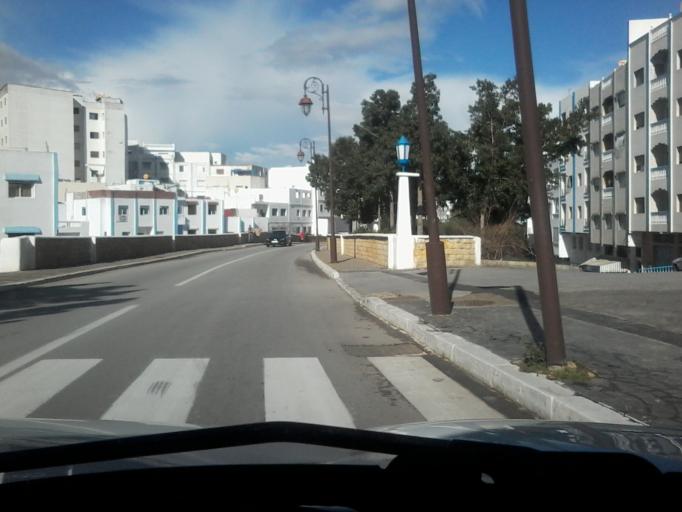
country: MA
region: Tanger-Tetouan
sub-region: Tetouan
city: Martil
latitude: 35.6863
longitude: -5.3308
